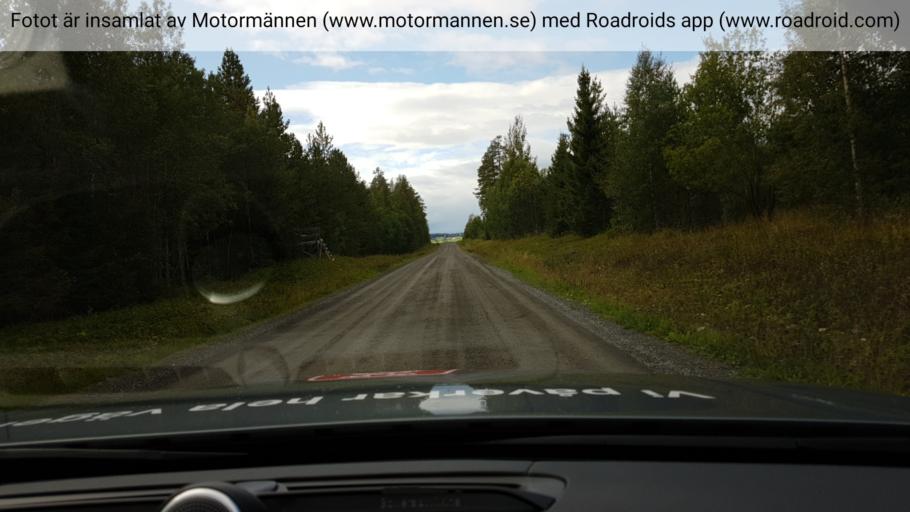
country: SE
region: Jaemtland
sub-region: OEstersunds Kommun
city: Lit
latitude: 63.6790
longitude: 14.8114
